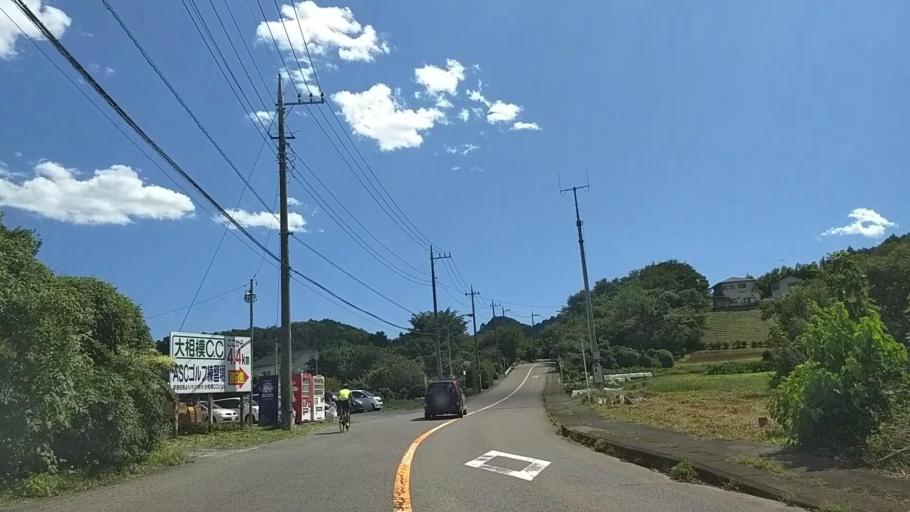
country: JP
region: Tokyo
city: Hachioji
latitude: 35.5704
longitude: 139.2812
